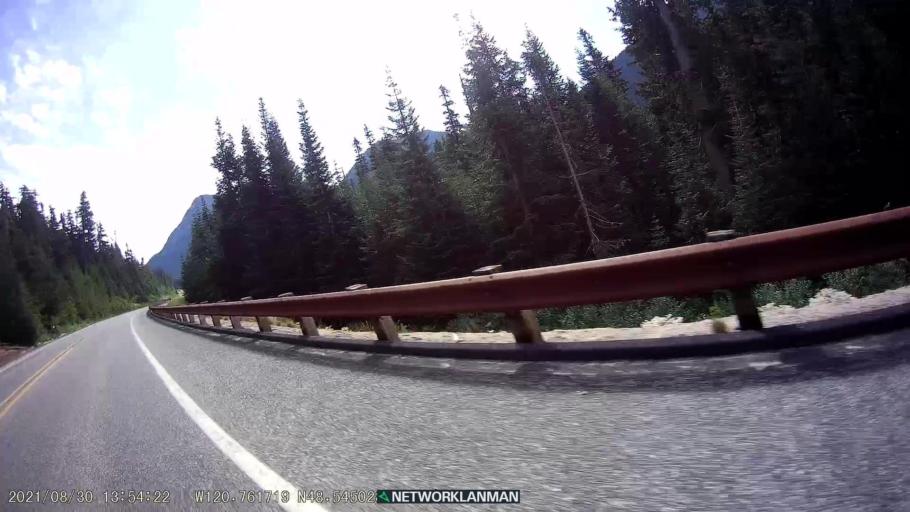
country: US
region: Washington
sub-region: Chelan County
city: Granite Falls
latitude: 48.5442
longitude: -120.7618
